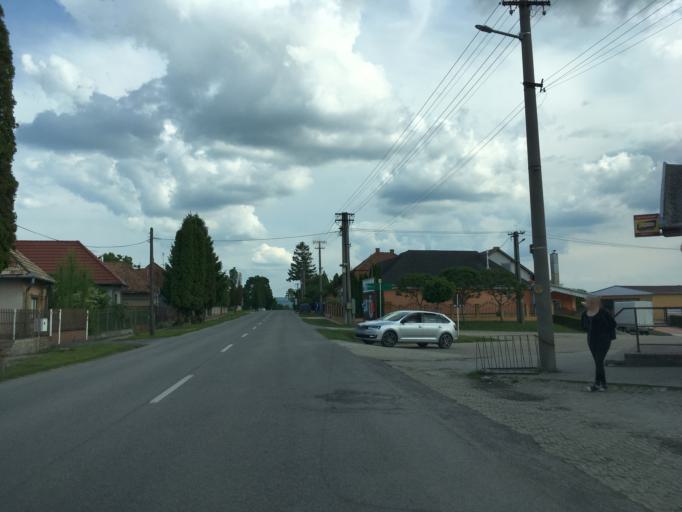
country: HU
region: Komarom-Esztergom
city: Dunaalmas
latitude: 47.7840
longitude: 18.2942
